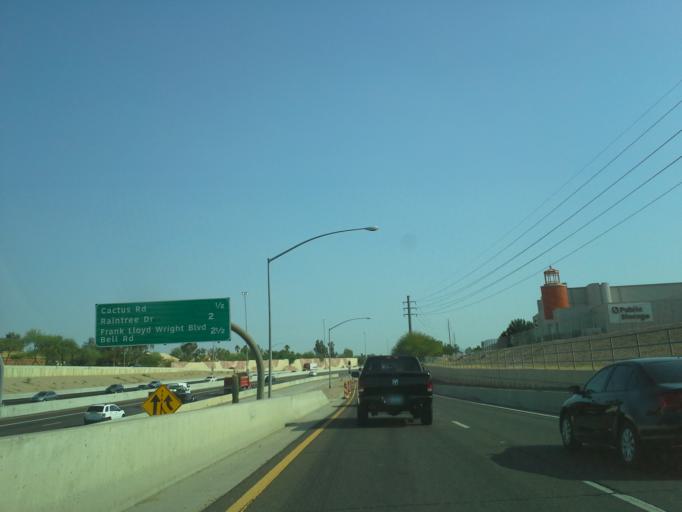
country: US
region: Arizona
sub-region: Maricopa County
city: Paradise Valley
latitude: 33.5835
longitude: -111.8910
